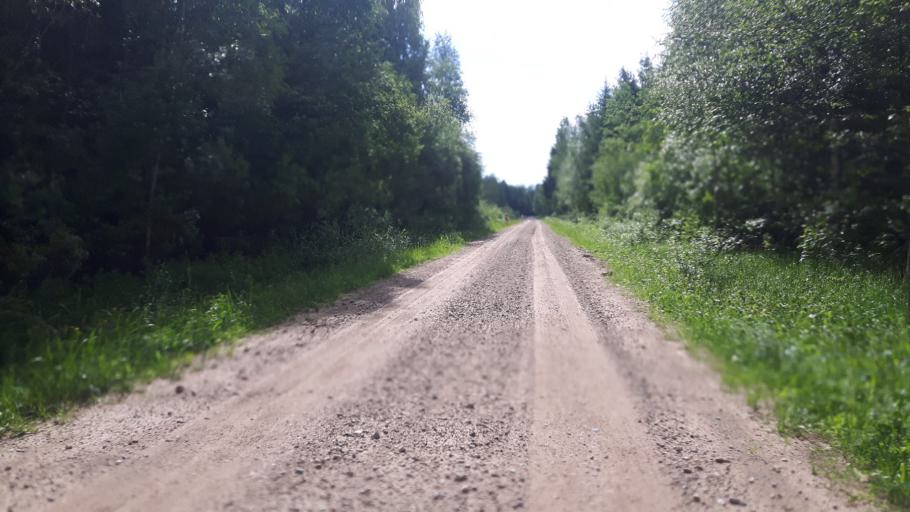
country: EE
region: Paernumaa
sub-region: Vaendra vald (alev)
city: Vandra
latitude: 58.7322
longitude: 25.0060
